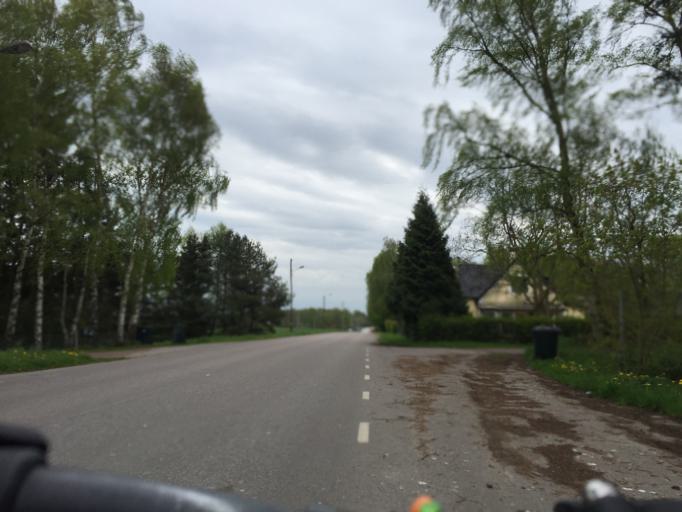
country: SE
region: Skane
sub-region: Lunds Kommun
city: Veberod
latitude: 55.6451
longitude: 13.4679
